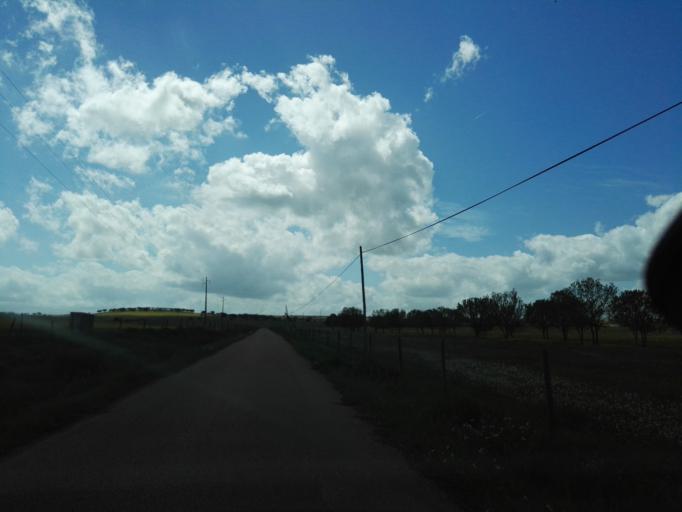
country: PT
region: Portalegre
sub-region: Elvas
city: Elvas
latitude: 38.9674
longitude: -7.1726
